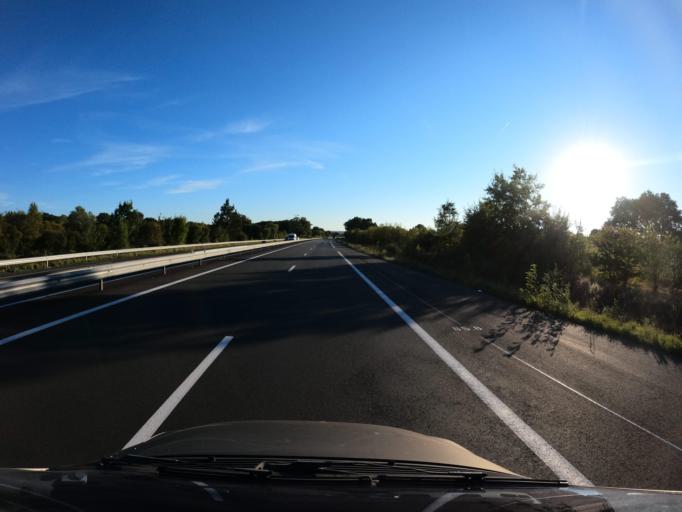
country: FR
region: Pays de la Loire
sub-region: Departement de la Vendee
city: Saint-Fulgent
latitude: 46.8504
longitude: -1.1457
